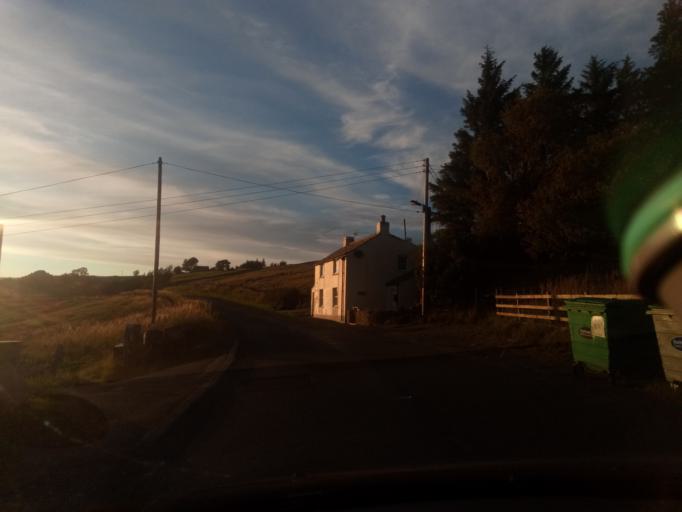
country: GB
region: England
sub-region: County Durham
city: Holwick
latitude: 54.7648
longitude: -2.2334
